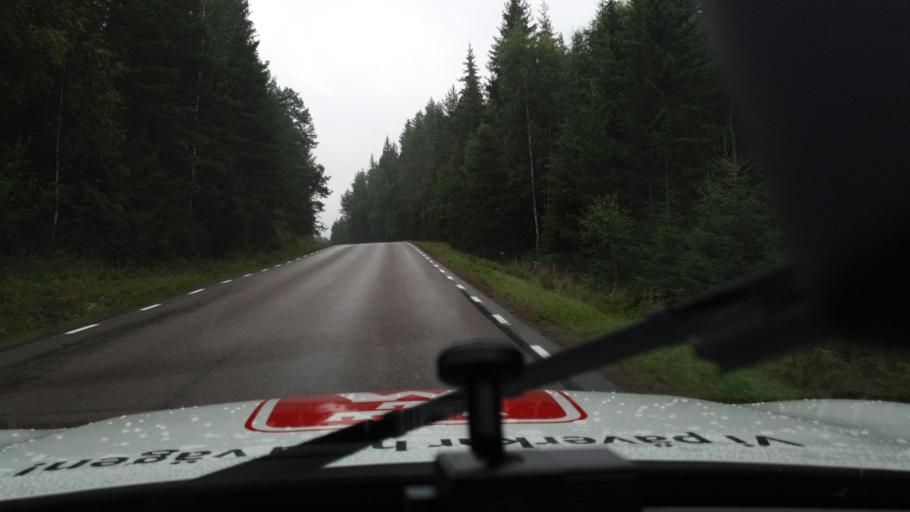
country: SE
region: Vaermland
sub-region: Eda Kommun
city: Charlottenberg
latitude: 59.8790
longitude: 12.3756
